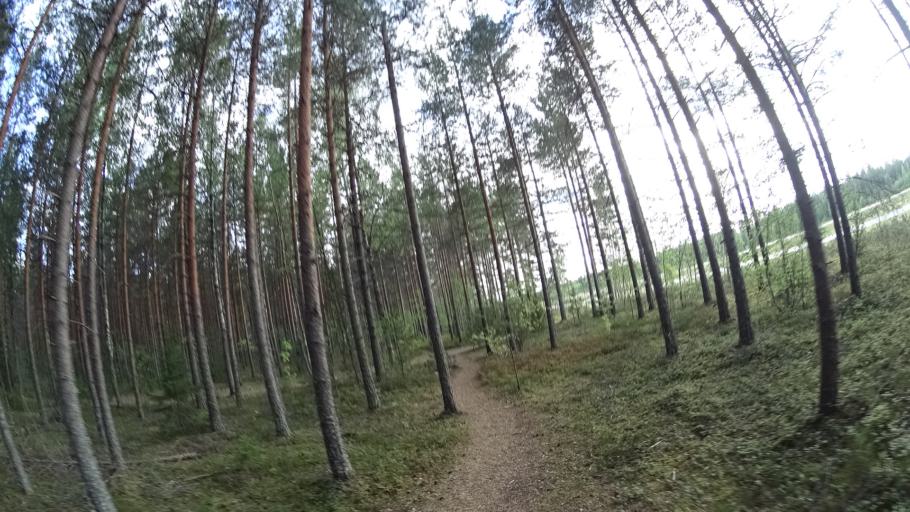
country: FI
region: Uusimaa
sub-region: Helsinki
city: Vihti
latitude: 60.3323
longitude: 24.2936
